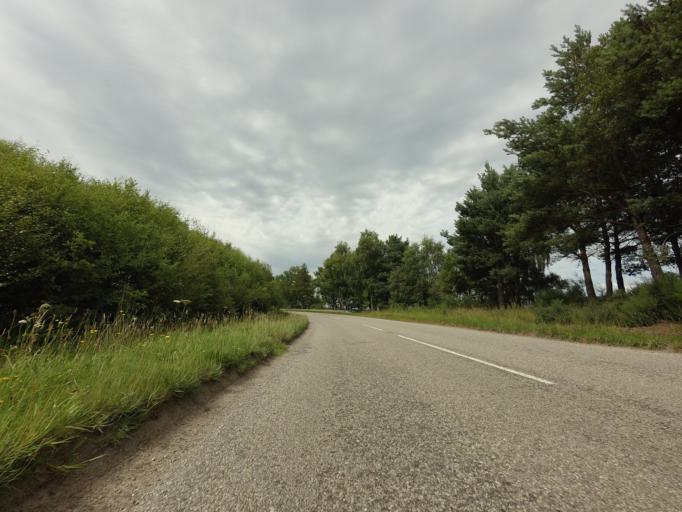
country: GB
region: Scotland
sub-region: Highland
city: Alness
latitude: 57.8615
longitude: -4.3172
